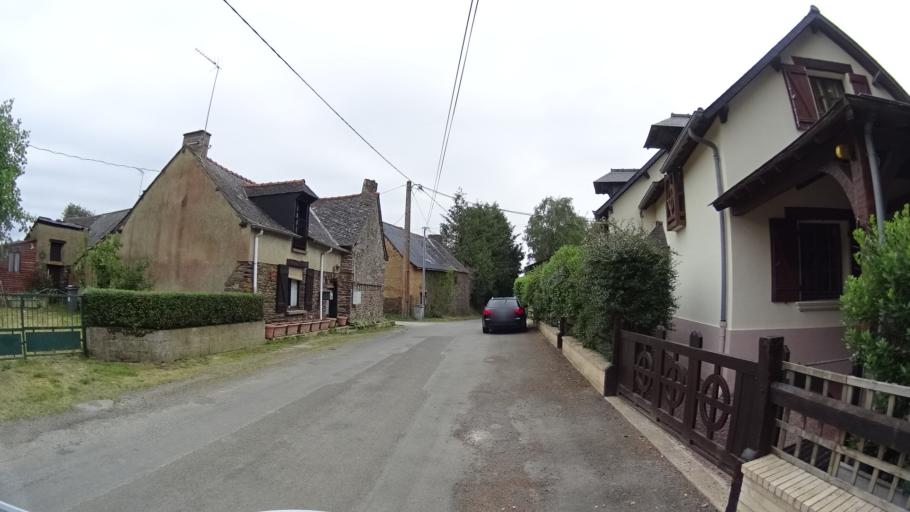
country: FR
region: Brittany
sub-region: Departement d'Ille-et-Vilaine
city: Orgeres
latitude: 47.9802
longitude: -1.6508
